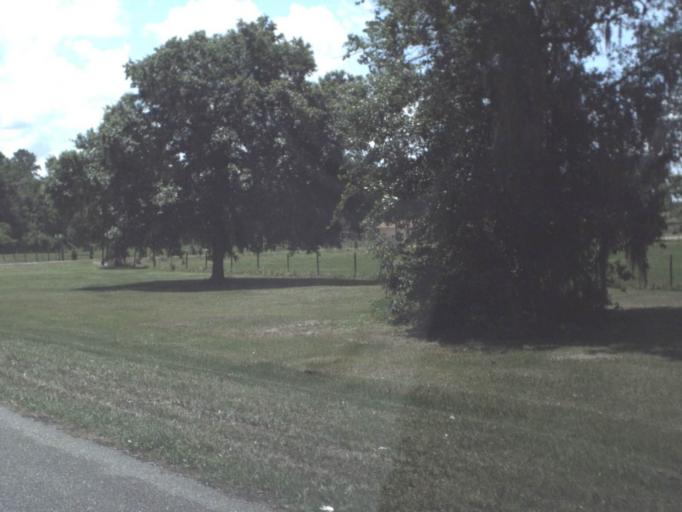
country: US
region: Florida
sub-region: Putnam County
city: Crescent City
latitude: 29.4614
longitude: -81.5226
